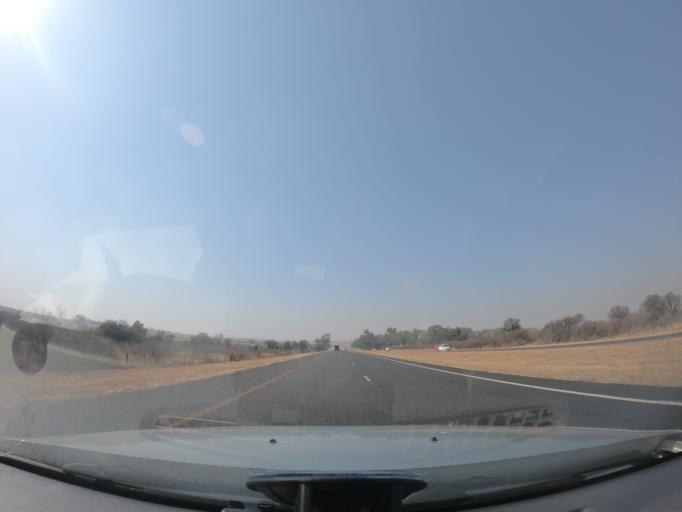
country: ZA
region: Gauteng
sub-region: City of Tshwane Metropolitan Municipality
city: Bronkhorstspruit
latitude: -25.8567
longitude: 28.8802
